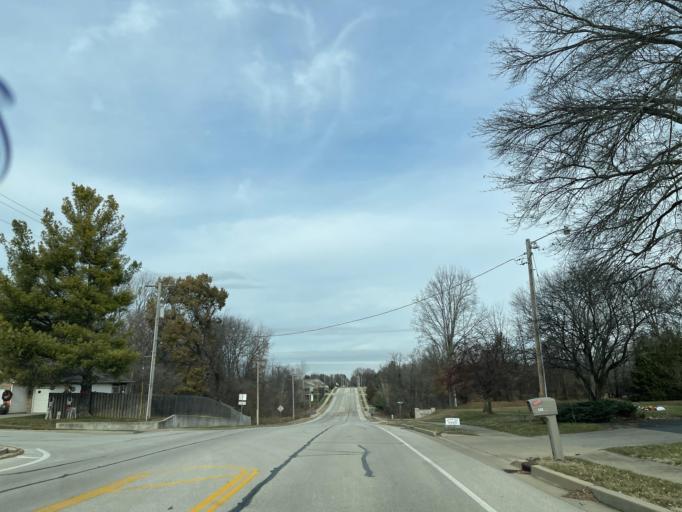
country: US
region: Illinois
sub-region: Sangamon County
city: Leland Grove
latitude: 39.7920
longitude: -89.7296
